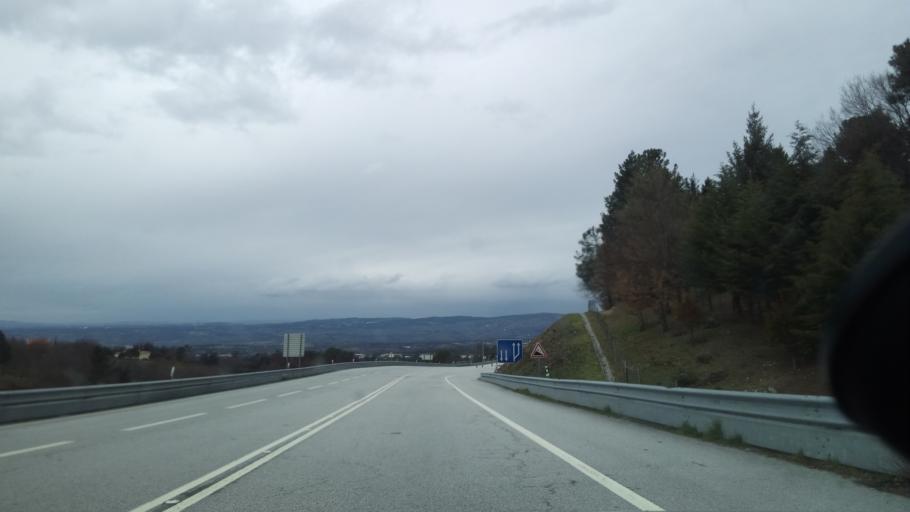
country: PT
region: Guarda
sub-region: Manteigas
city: Manteigas
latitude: 40.4823
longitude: -7.5970
